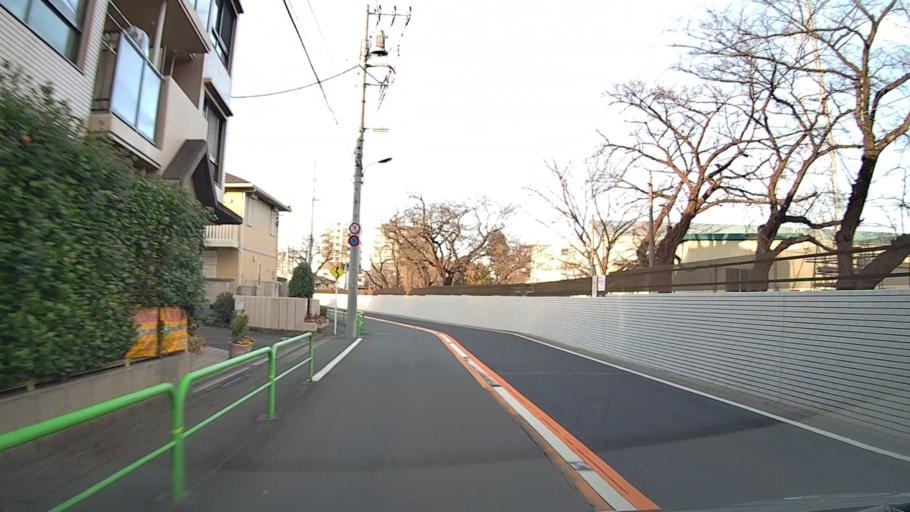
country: JP
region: Saitama
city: Wako
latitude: 35.7635
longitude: 139.6564
